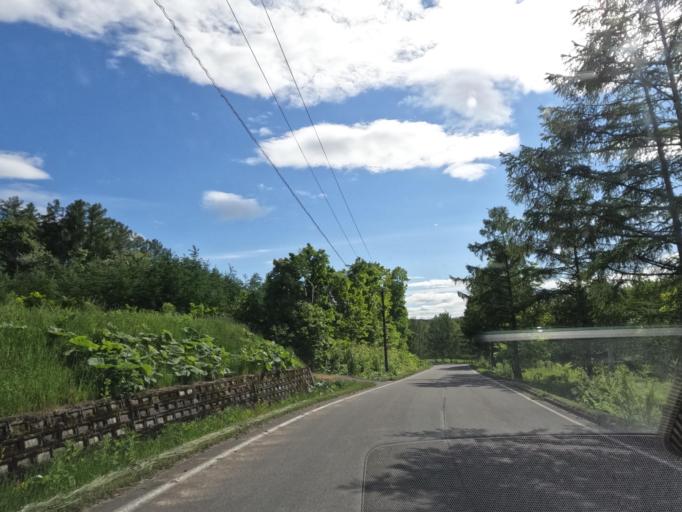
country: JP
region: Hokkaido
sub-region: Asahikawa-shi
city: Asahikawa
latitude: 43.7589
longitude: 142.5254
